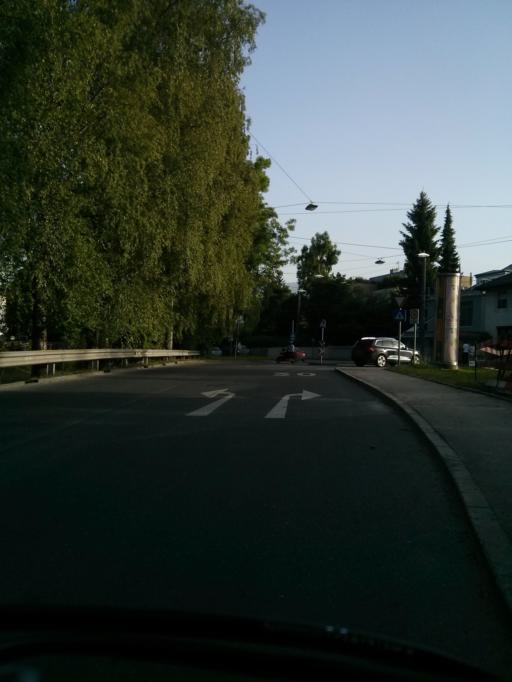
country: AT
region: Salzburg
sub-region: Salzburg Stadt
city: Salzburg
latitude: 47.8070
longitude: 13.0189
